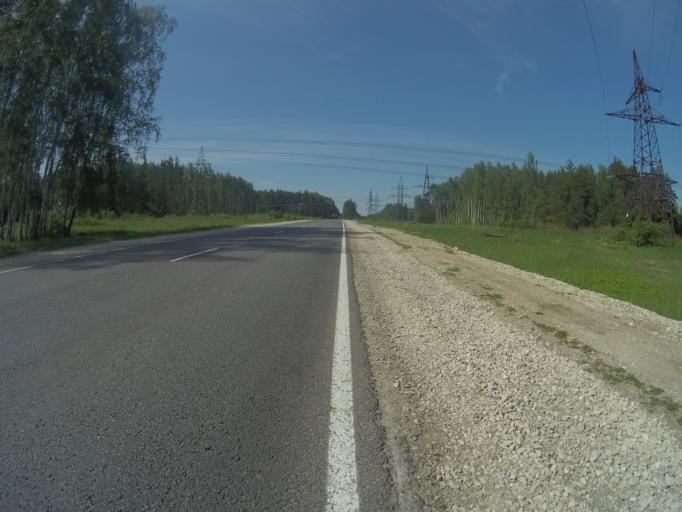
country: RU
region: Vladimir
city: Vorsha
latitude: 56.0753
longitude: 40.1117
